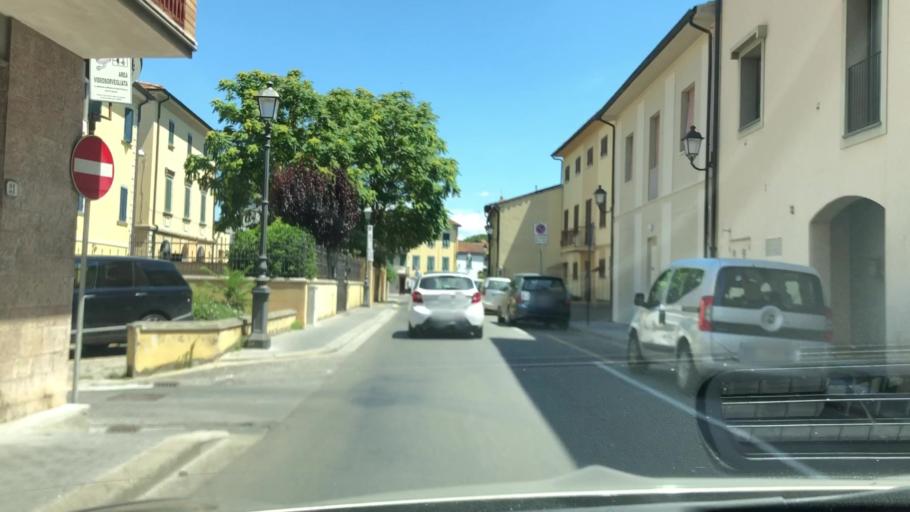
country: IT
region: Tuscany
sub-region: Province of Pisa
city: Ponsacco
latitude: 43.6196
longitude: 10.6319
